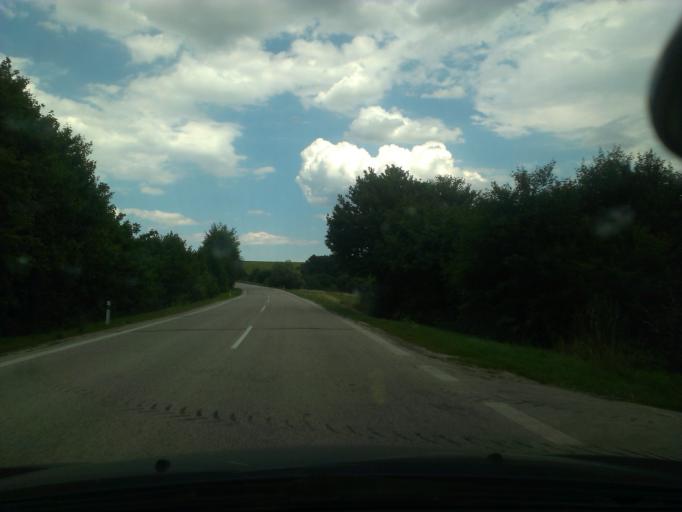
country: SK
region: Trenciansky
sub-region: Okres Myjava
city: Myjava
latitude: 48.7568
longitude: 17.5979
